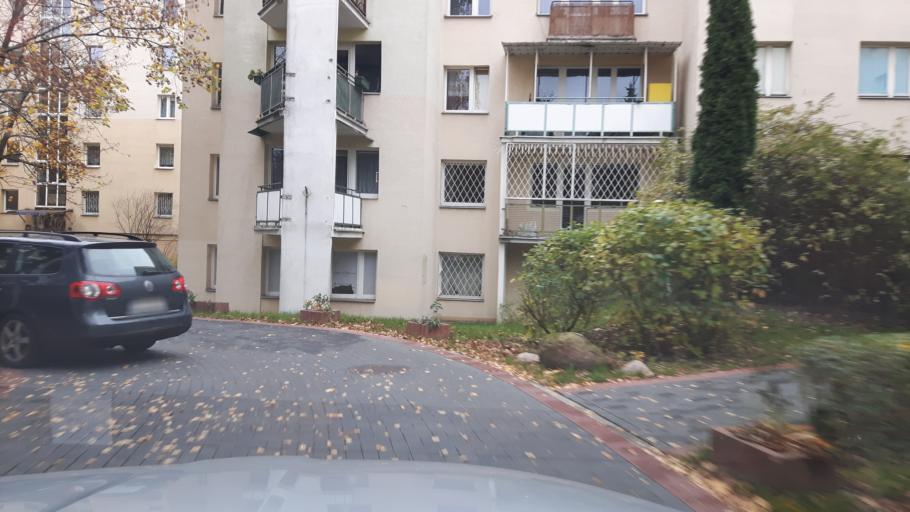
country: PL
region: Masovian Voivodeship
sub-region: Warszawa
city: Ursynow
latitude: 52.1527
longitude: 21.0260
